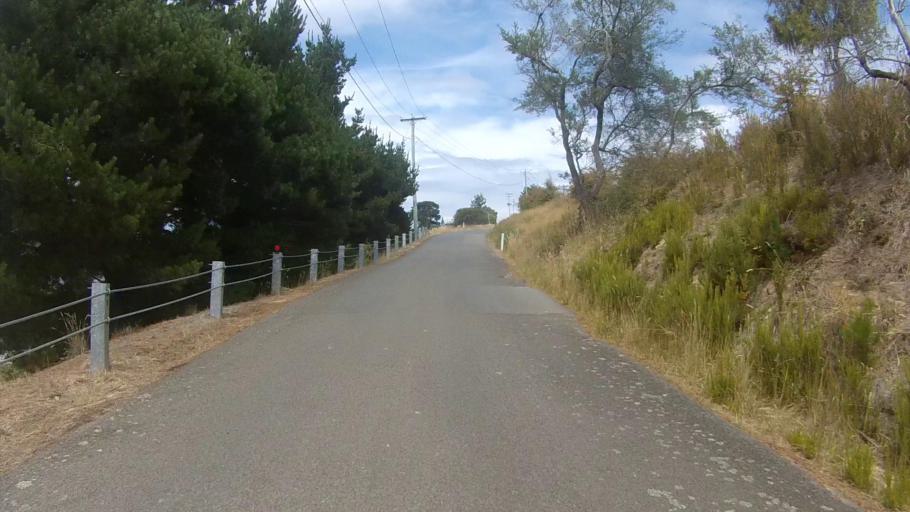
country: AU
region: Tasmania
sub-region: Kingborough
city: Blackmans Bay
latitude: -43.0551
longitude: 147.3276
